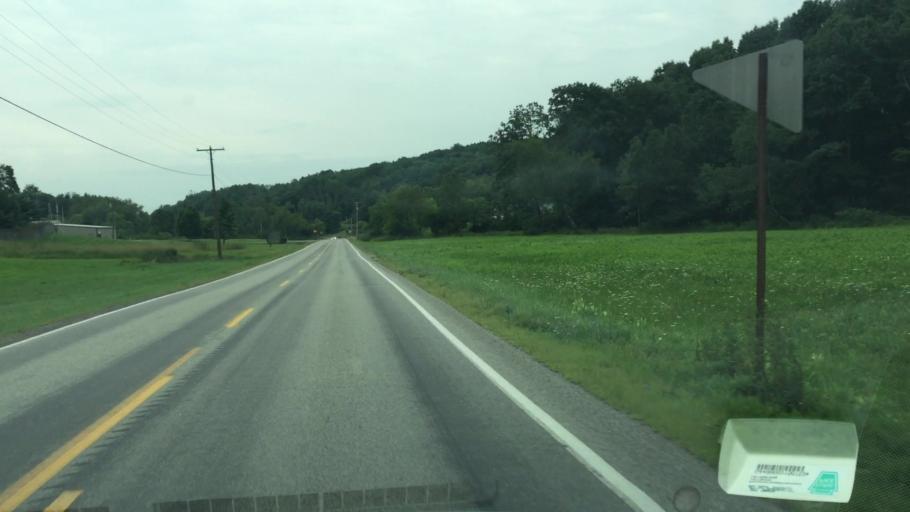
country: US
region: Pennsylvania
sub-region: Allegheny County
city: Curtisville
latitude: 40.6951
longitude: -79.8403
